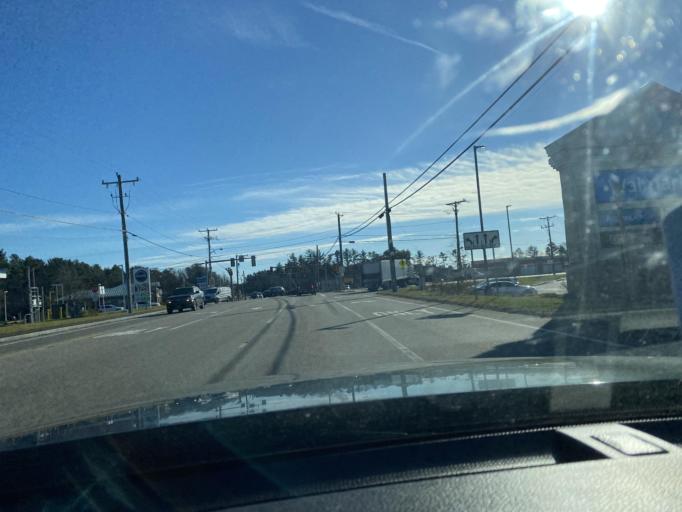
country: US
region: Massachusetts
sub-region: Plymouth County
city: West Wareham
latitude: 41.7819
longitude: -70.7444
